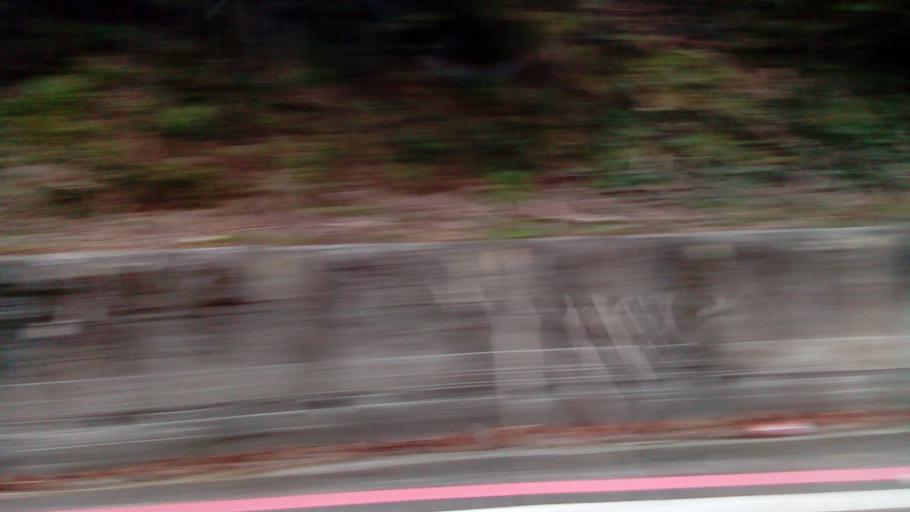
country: TW
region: Taiwan
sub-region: Hualien
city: Hualian
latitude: 24.3861
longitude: 121.3478
